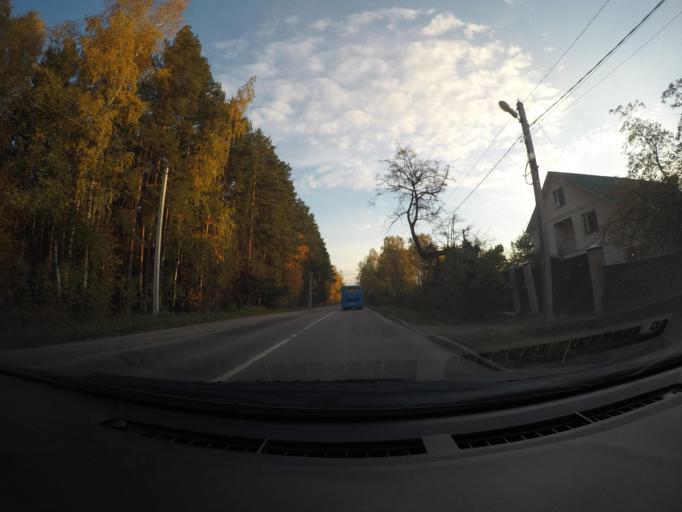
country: RU
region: Moskovskaya
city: Firsanovka
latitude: 55.9420
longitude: 37.2499
